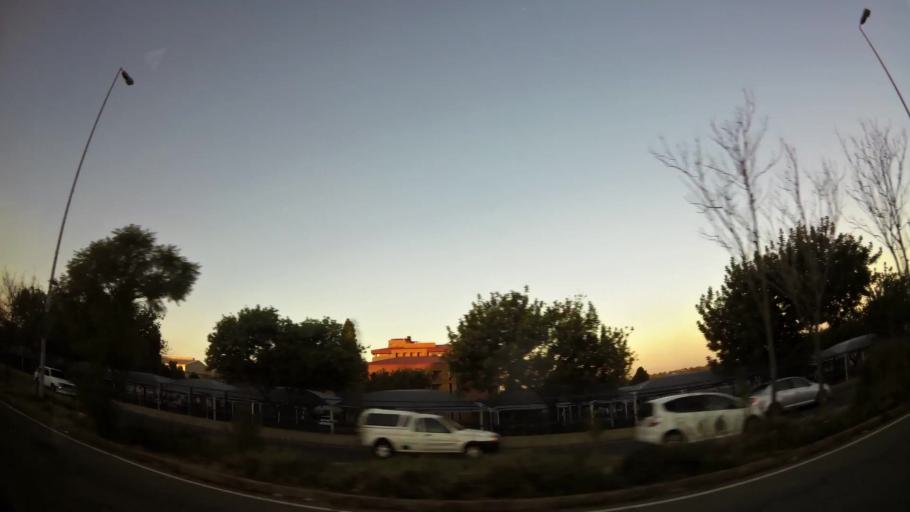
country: ZA
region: Gauteng
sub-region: City of Johannesburg Metropolitan Municipality
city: Roodepoort
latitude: -26.1577
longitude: 27.9004
